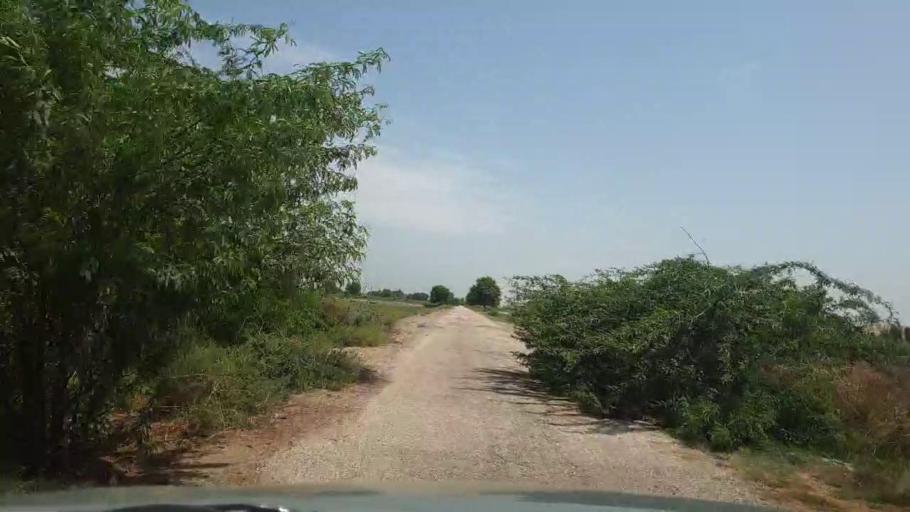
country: PK
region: Sindh
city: Bozdar
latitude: 27.0927
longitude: 68.9697
